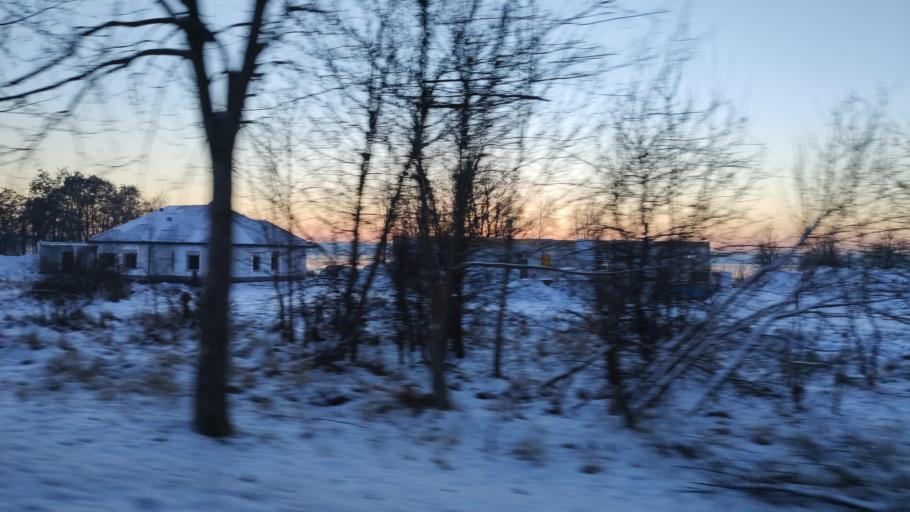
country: PL
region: Kujawsko-Pomorskie
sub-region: Powiat zninski
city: Barcin
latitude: 52.8714
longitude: 17.9009
